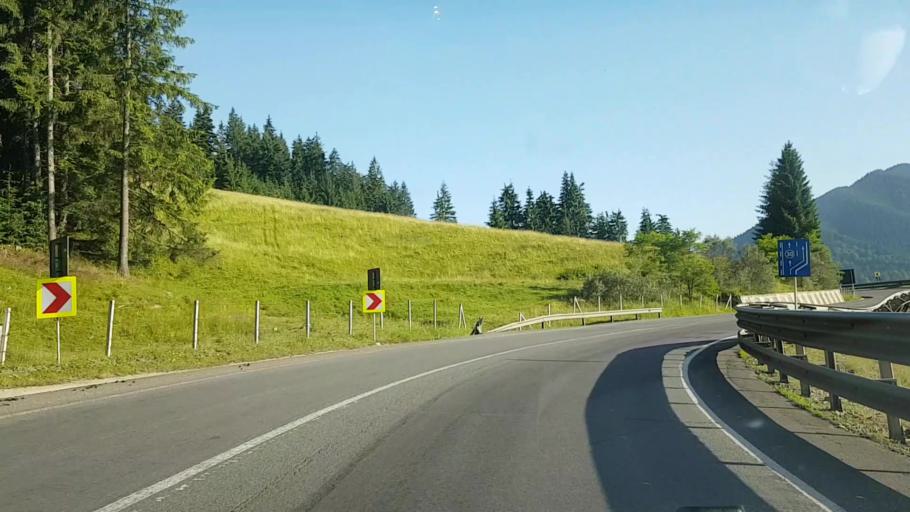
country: RO
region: Bistrita-Nasaud
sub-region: Comuna Lunca Ilvei
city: Lunca Ilvei
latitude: 47.2318
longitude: 24.9676
